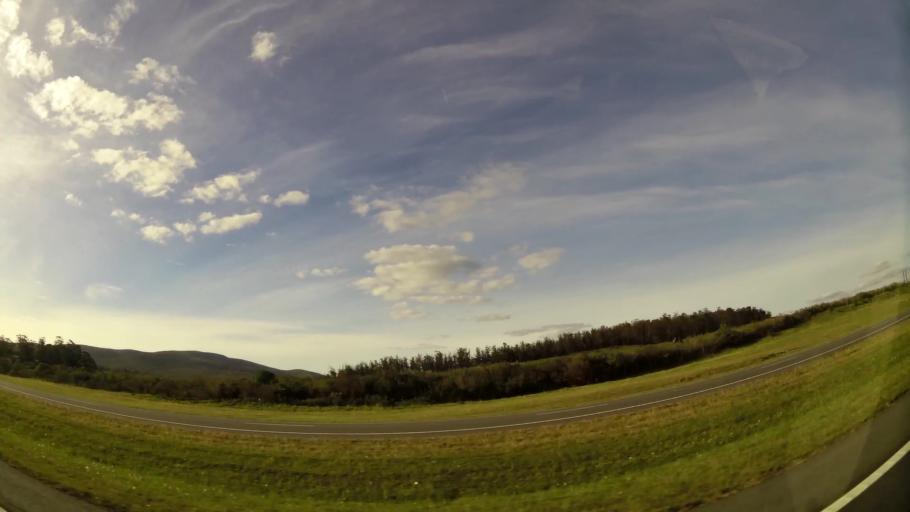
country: UY
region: Maldonado
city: Pan de Azucar
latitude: -34.7861
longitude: -55.2783
